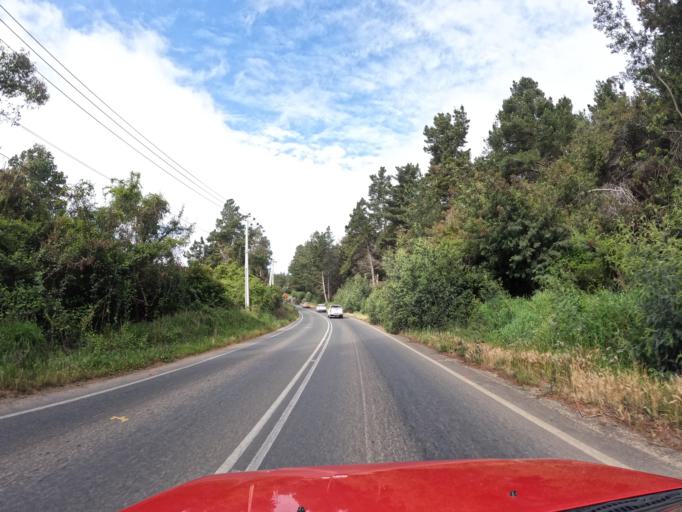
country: CL
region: O'Higgins
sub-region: Provincia de Colchagua
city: Santa Cruz
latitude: -34.3550
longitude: -71.9117
